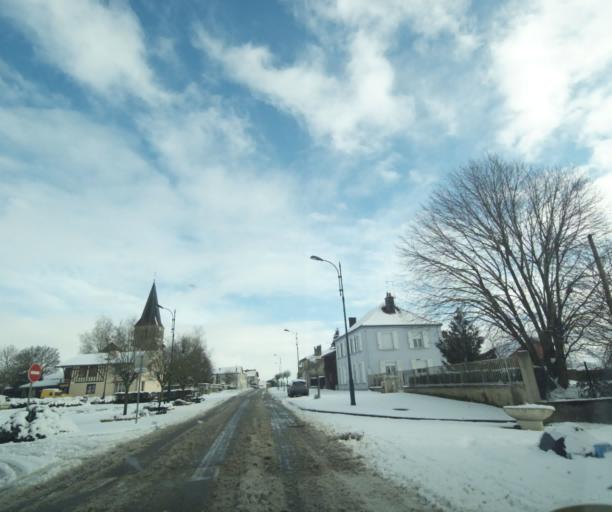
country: FR
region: Champagne-Ardenne
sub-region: Departement de la Haute-Marne
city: Montier-en-Der
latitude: 48.4545
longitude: 4.6869
